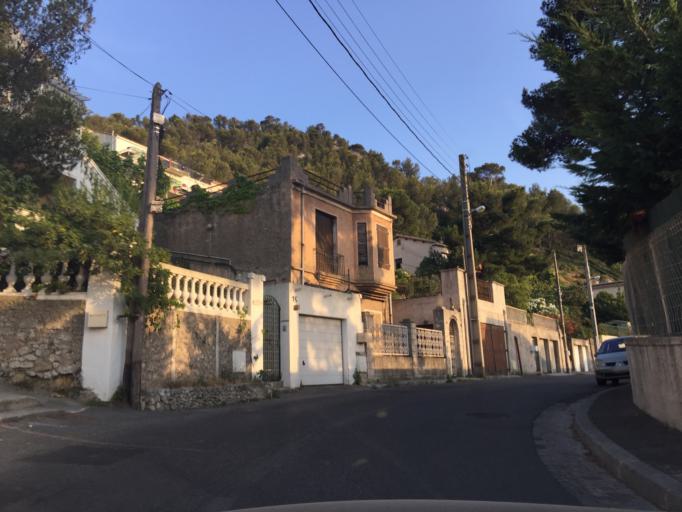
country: FR
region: Provence-Alpes-Cote d'Azur
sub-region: Departement des Bouches-du-Rhone
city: Marseille 09
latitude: 43.2447
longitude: 5.4227
